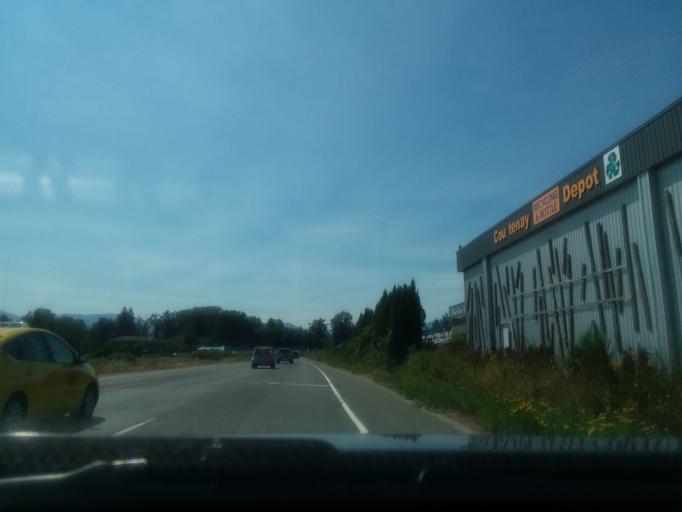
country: CA
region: British Columbia
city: Courtenay
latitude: 49.6952
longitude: -124.9887
